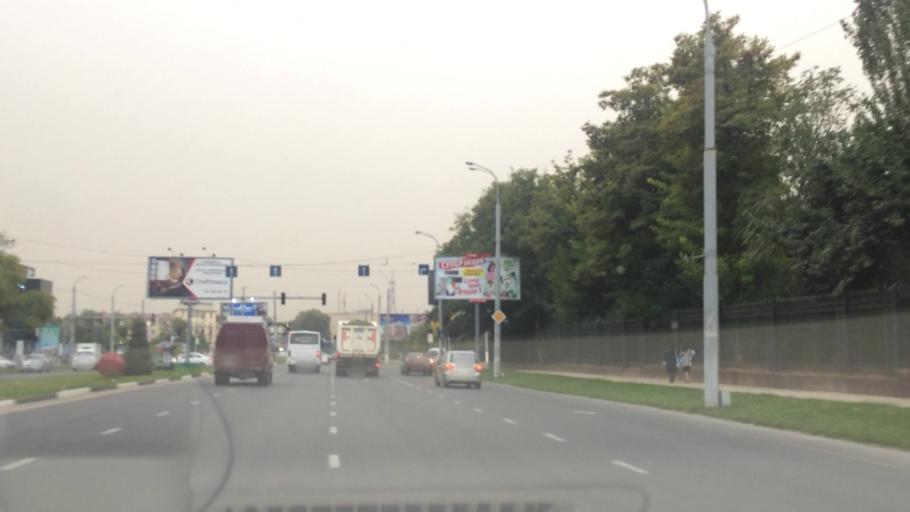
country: UZ
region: Toshkent Shahri
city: Tashkent
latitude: 41.3029
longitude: 69.2480
